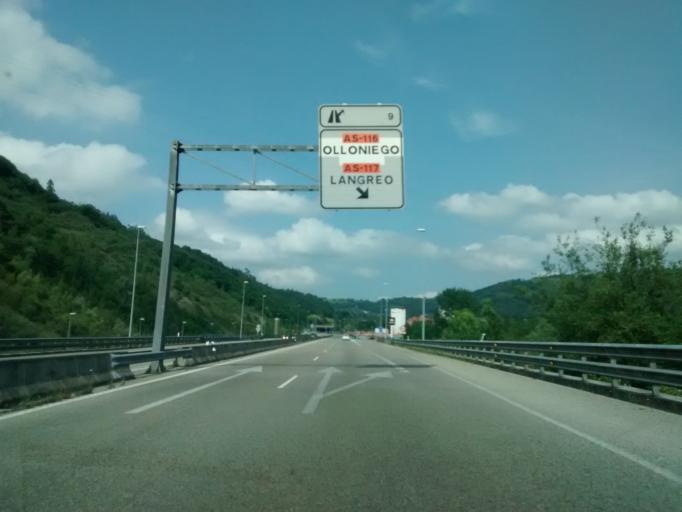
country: ES
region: Asturias
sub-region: Province of Asturias
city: Sama
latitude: 43.3235
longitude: -5.7354
